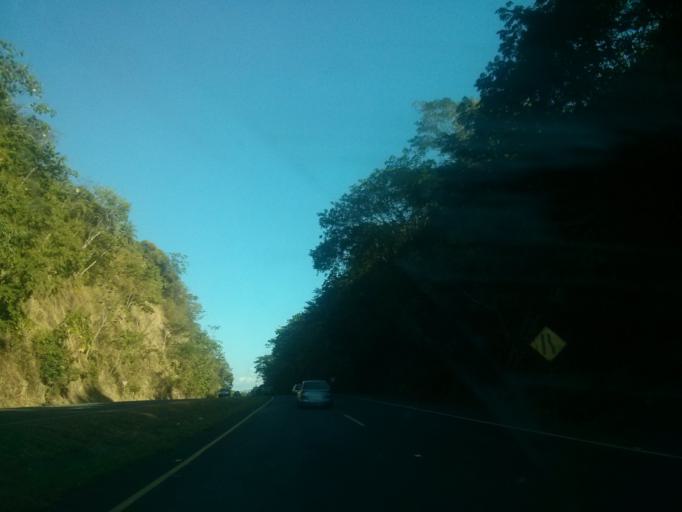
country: CR
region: Alajuela
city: Orotina
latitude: 9.9002
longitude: -84.5419
